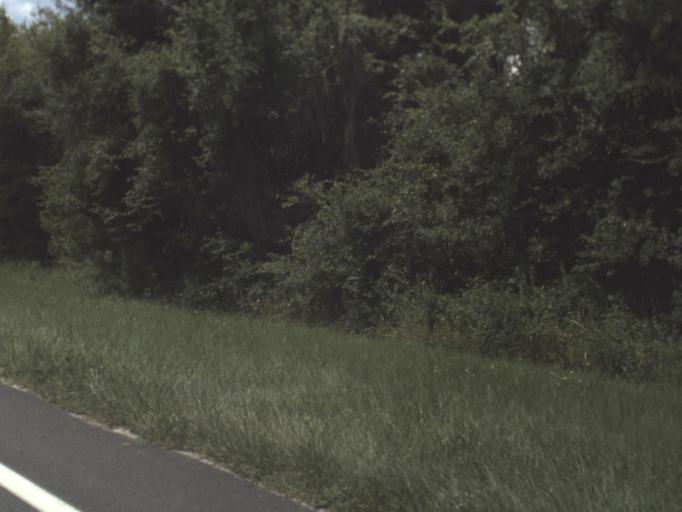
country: US
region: Florida
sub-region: Hamilton County
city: Jasper
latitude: 30.4124
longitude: -82.8476
